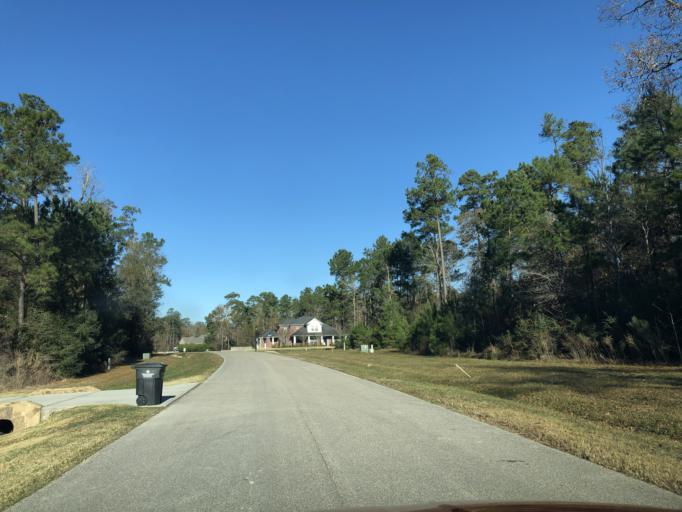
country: US
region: Texas
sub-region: Montgomery County
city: Porter Heights
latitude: 30.0666
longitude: -95.3230
